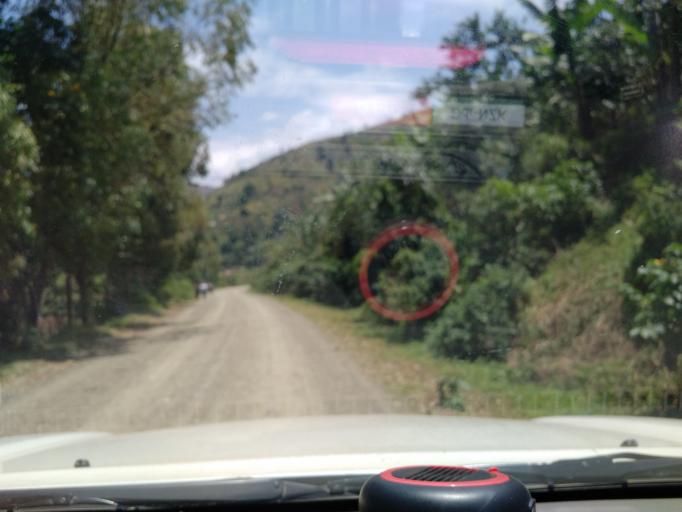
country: CD
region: Nord Kivu
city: Sake
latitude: -1.7804
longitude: 29.0101
